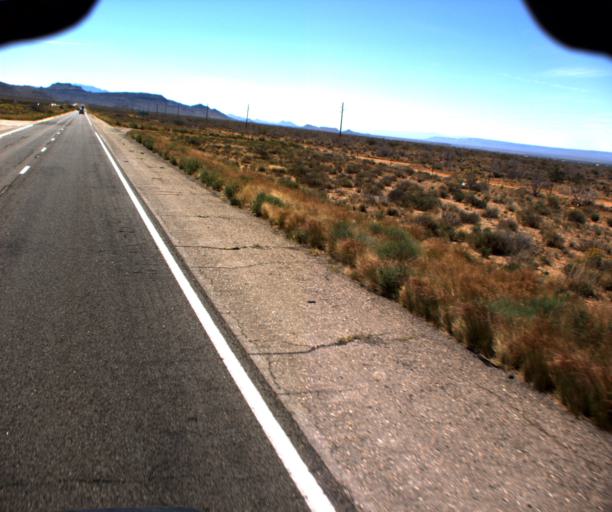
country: US
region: Arizona
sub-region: Mohave County
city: Golden Valley
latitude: 35.2817
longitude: -114.1762
